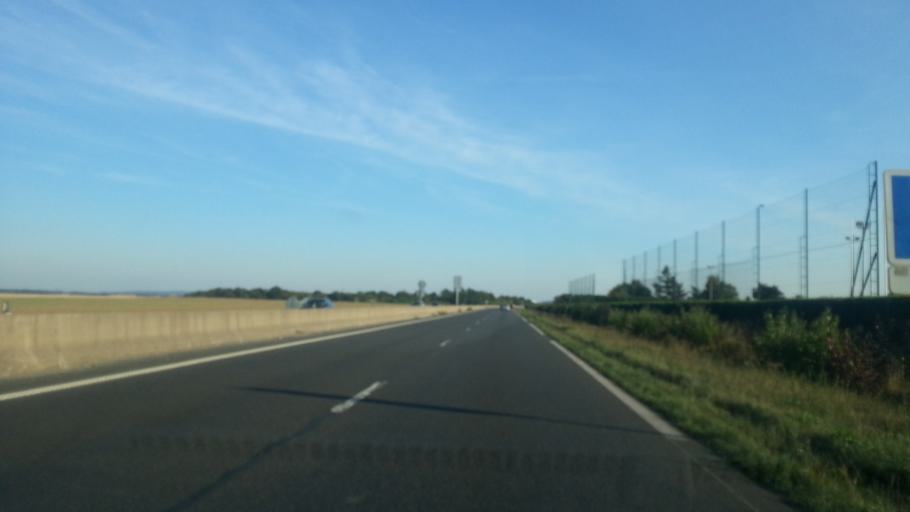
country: FR
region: Picardie
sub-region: Departement de l'Oise
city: Tille
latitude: 49.4462
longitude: 2.1071
